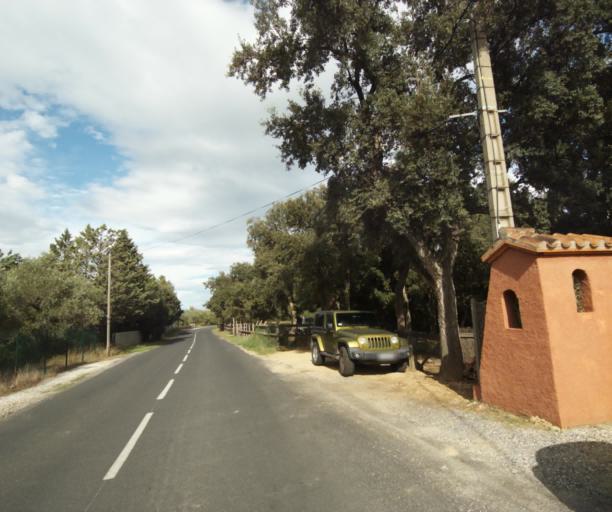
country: FR
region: Languedoc-Roussillon
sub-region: Departement des Pyrenees-Orientales
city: Argelers
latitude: 42.5388
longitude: 2.9990
